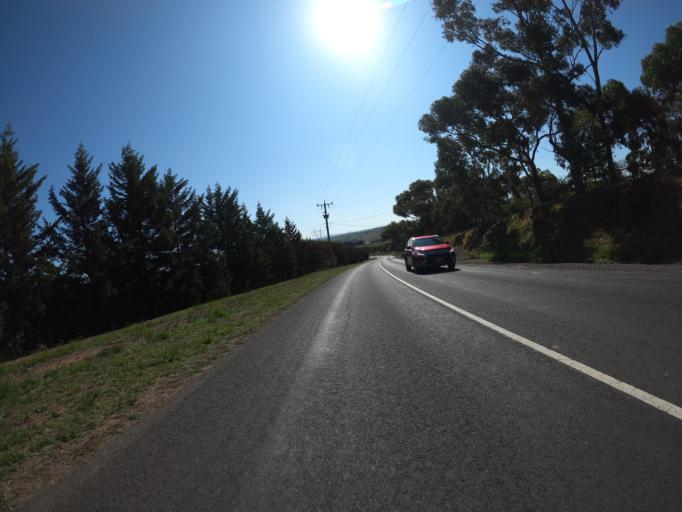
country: AU
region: Victoria
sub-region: Hume
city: Greenvale
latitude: -37.5513
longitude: 144.8629
